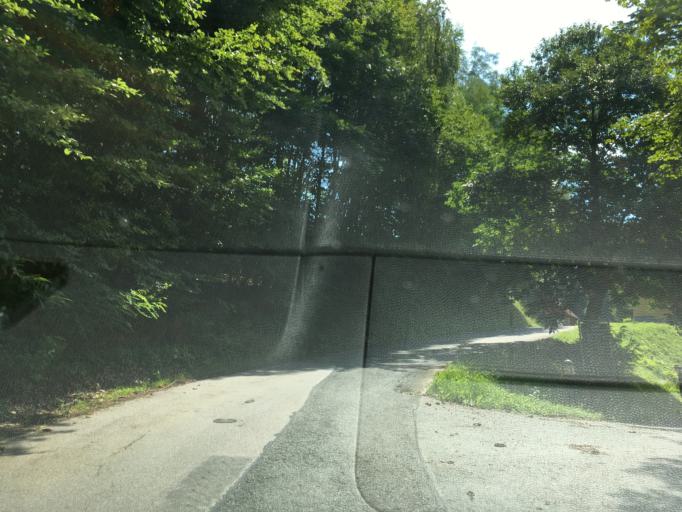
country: AT
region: Styria
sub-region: Politischer Bezirk Leibnitz
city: Kitzeck im Sausal
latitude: 46.7909
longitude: 15.4230
